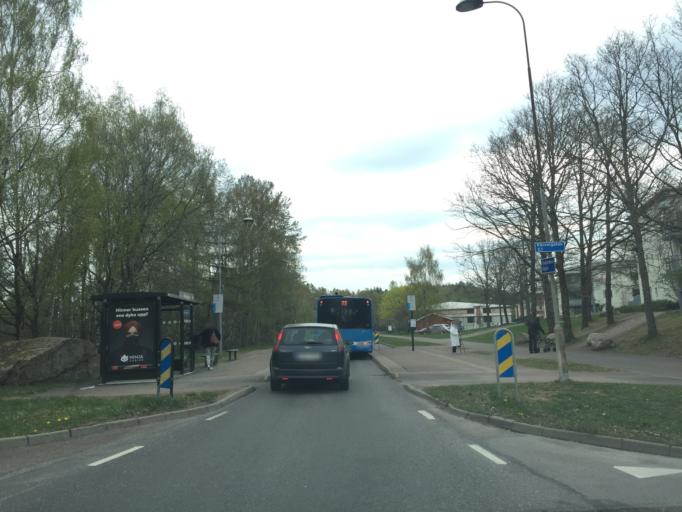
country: SE
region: Vaestra Goetaland
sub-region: Goteborg
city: Loevgaerdet
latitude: 57.8179
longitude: 12.0307
